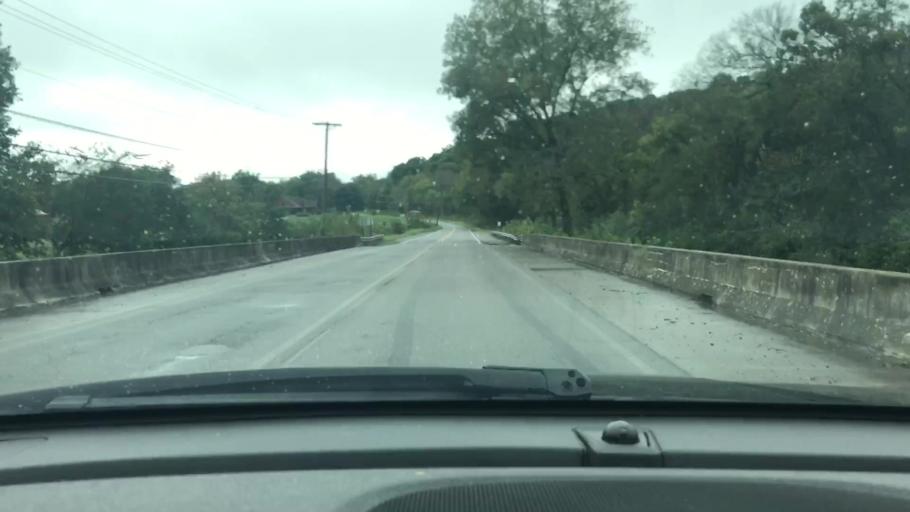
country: US
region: Tennessee
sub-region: Cheatham County
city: Kingston Springs
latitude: 36.1009
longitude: -87.1263
